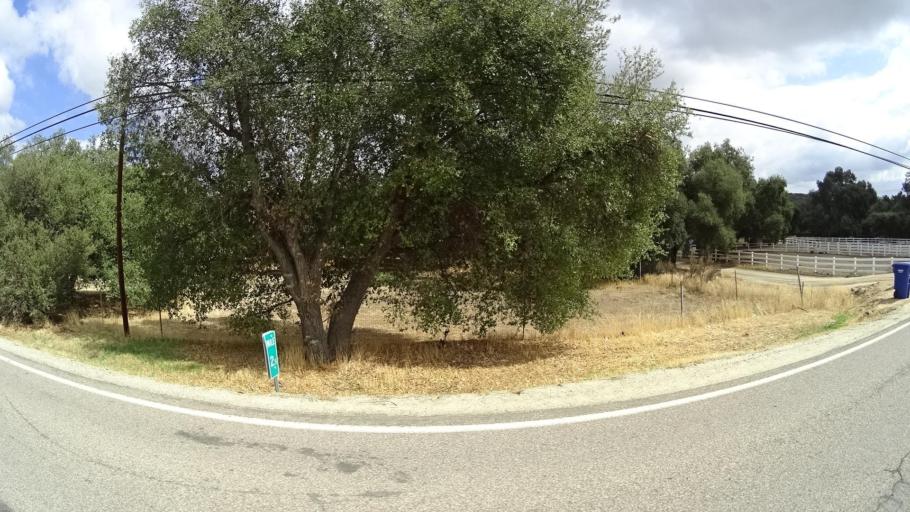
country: US
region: California
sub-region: San Diego County
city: Campo
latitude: 32.6606
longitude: -116.4879
